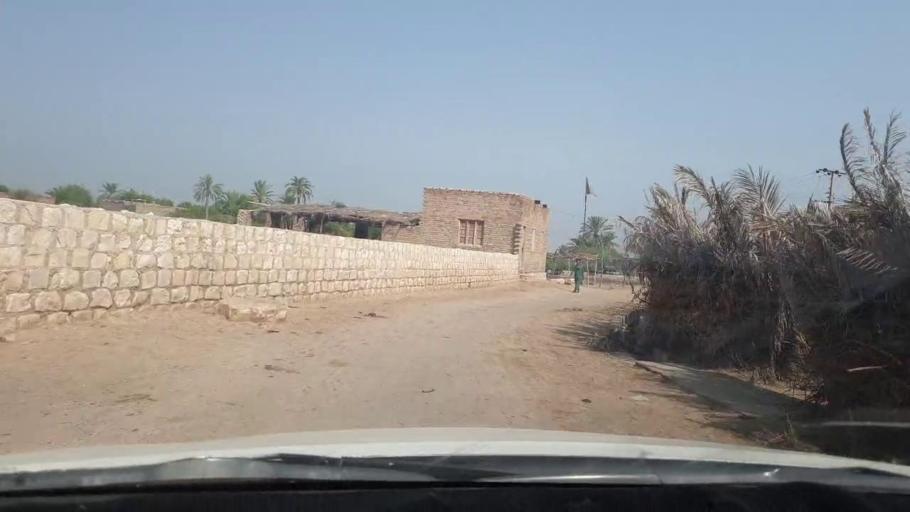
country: PK
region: Sindh
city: Rohri
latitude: 27.6304
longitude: 68.8858
